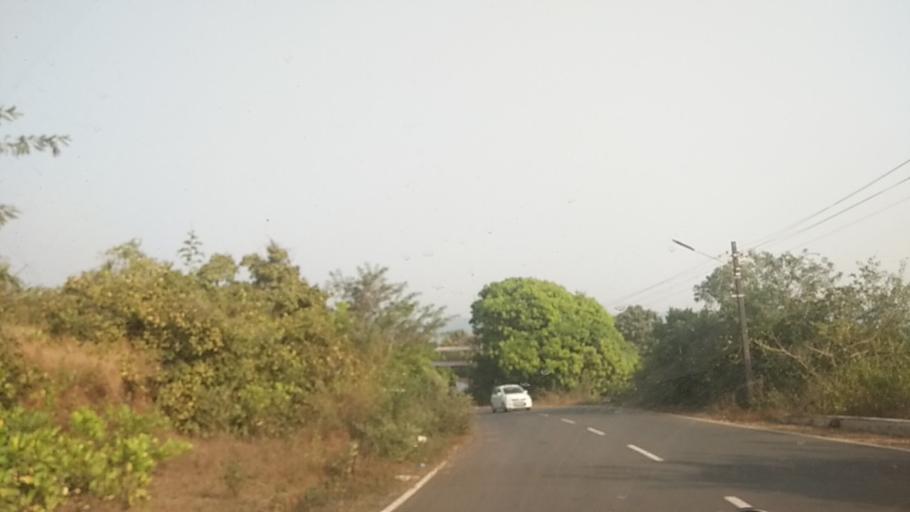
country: IN
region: Goa
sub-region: North Goa
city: Morjim
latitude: 15.6489
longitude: 73.7619
